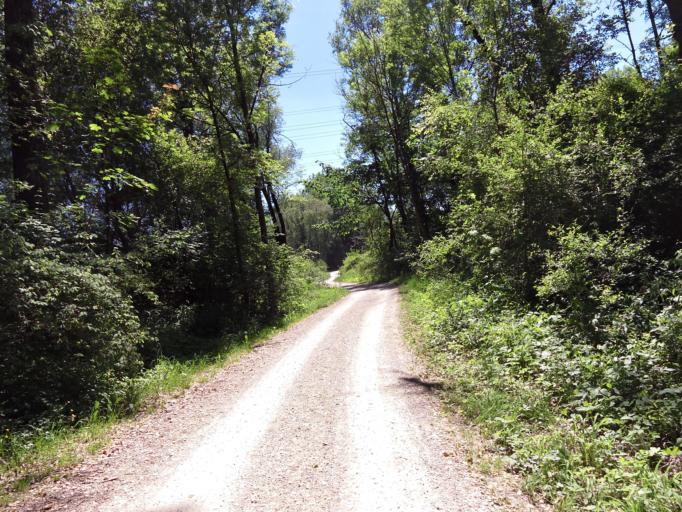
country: DE
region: Bavaria
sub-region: Upper Bavaria
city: Ismaning
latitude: 48.2770
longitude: 11.6915
